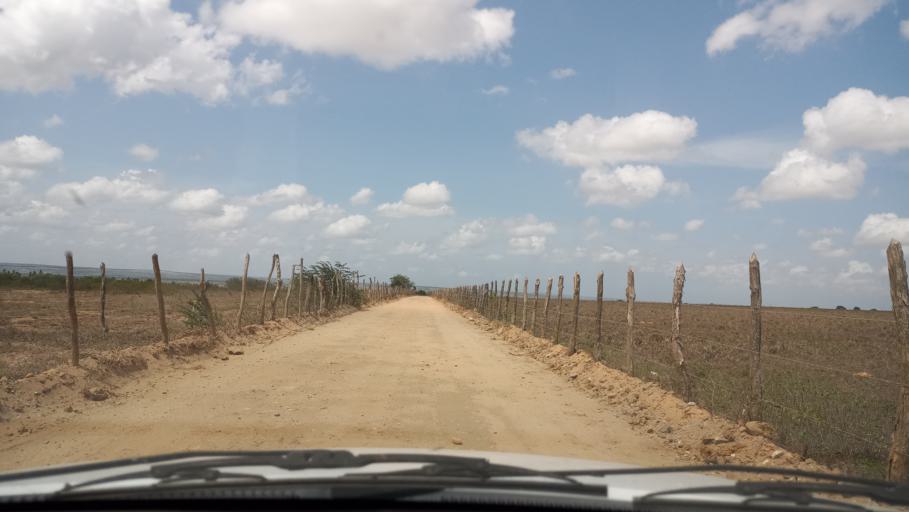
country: BR
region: Rio Grande do Norte
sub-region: Montanhas
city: Montanhas
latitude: -6.3529
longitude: -35.3341
